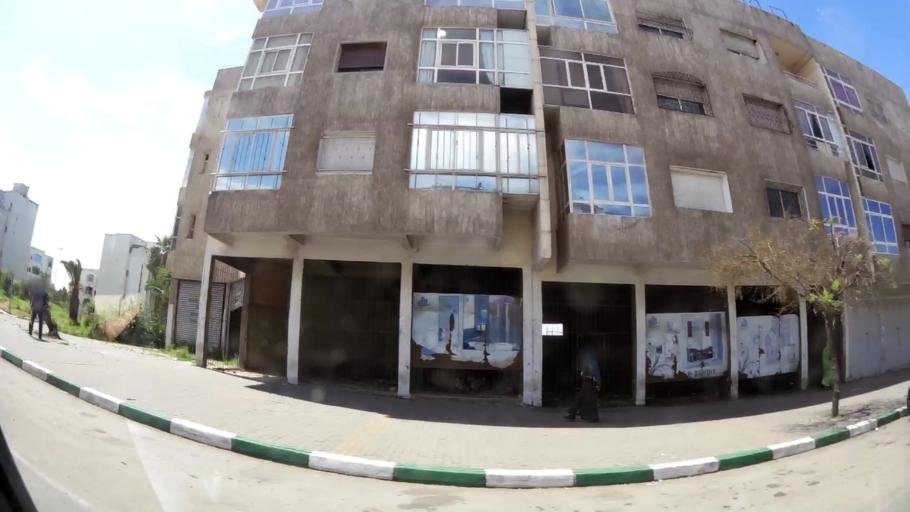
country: MA
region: Grand Casablanca
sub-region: Mediouna
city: Tit Mellil
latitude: 33.6033
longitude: -7.5197
